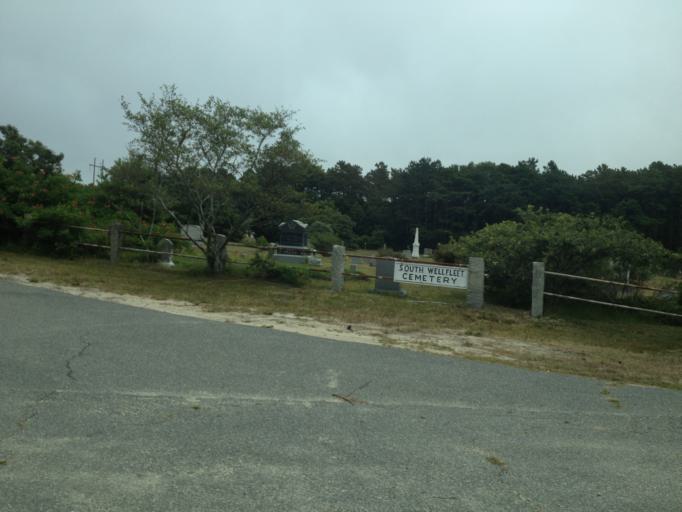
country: US
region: Massachusetts
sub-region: Barnstable County
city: North Eastham
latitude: 41.9083
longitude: -69.9860
